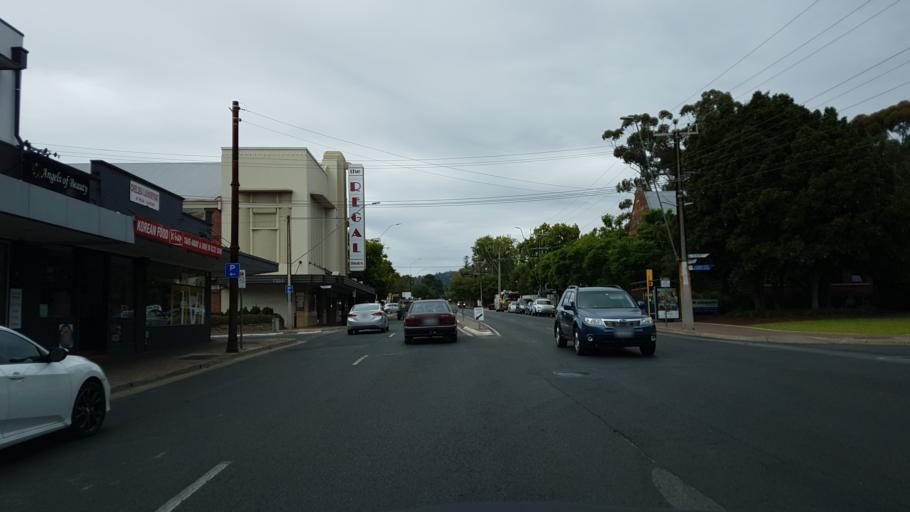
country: AU
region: South Australia
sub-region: Burnside
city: Leabrook
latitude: -34.9263
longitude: 138.6509
